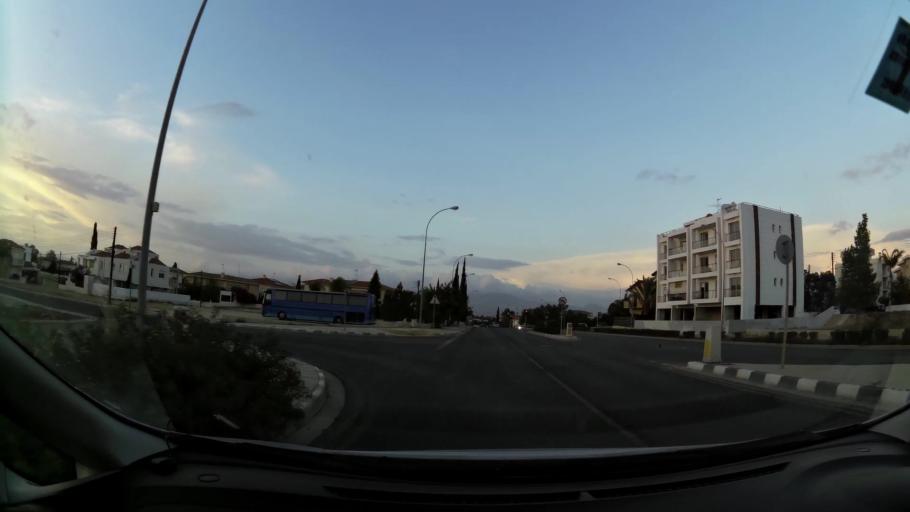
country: CY
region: Lefkosia
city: Nicosia
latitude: 35.1518
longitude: 33.3818
